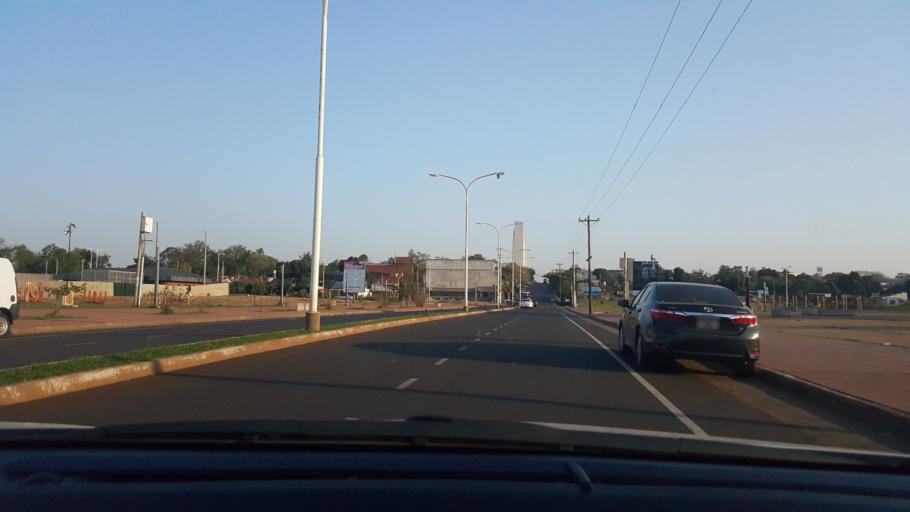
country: AR
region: Misiones
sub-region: Departamento de Capital
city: Posadas
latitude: -27.3775
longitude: -55.8876
